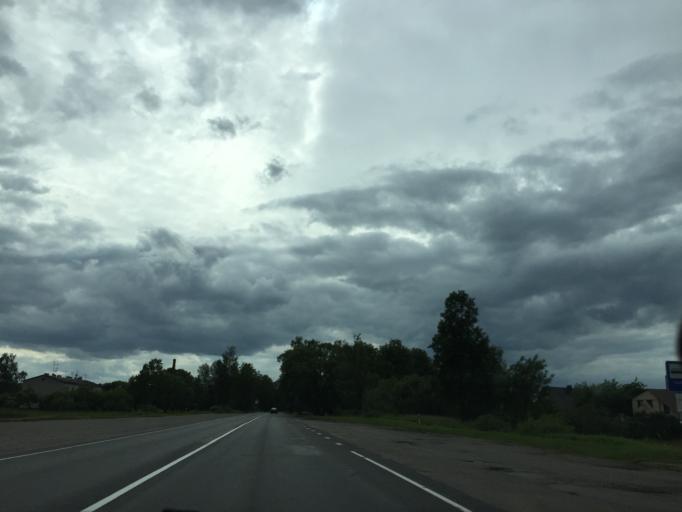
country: LV
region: Apes Novads
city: Ape
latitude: 57.4559
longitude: 26.3747
